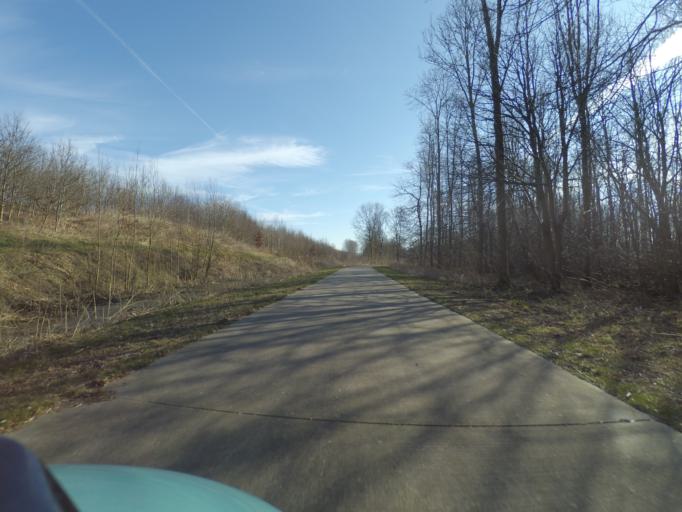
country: NL
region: Flevoland
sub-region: Gemeente Almere
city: Almere Stad
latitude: 52.4051
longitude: 5.3306
